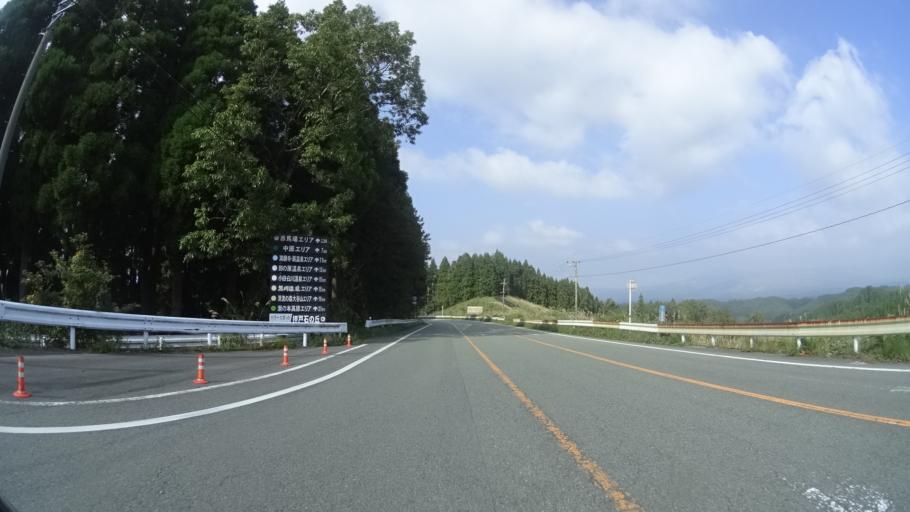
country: JP
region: Kumamoto
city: Aso
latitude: 33.0506
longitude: 131.0675
